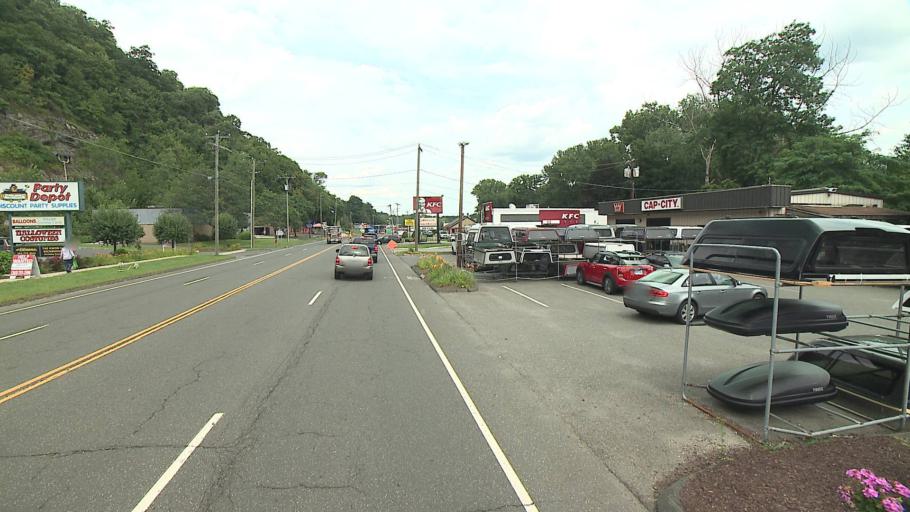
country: US
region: Connecticut
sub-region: Fairfield County
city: Danbury
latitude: 41.4300
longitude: -73.4160
